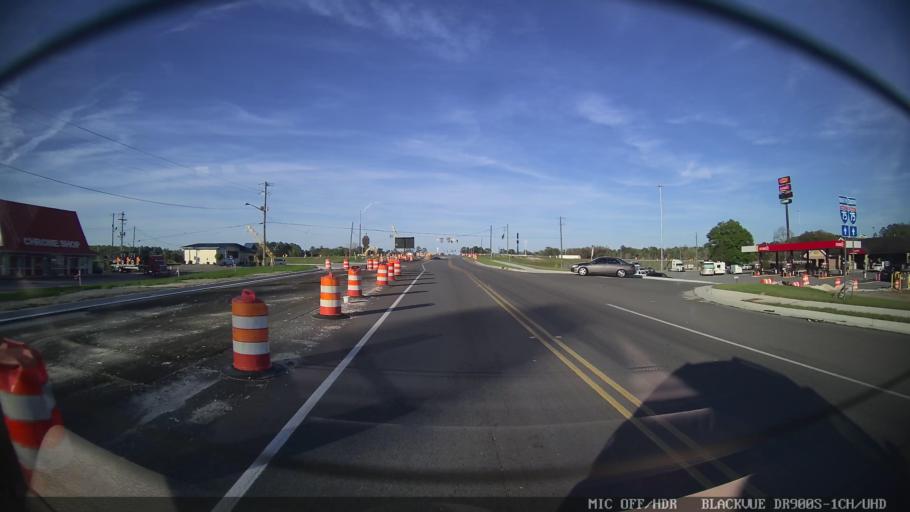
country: US
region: Georgia
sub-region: Echols County
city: Statenville
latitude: 30.6419
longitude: -83.1911
